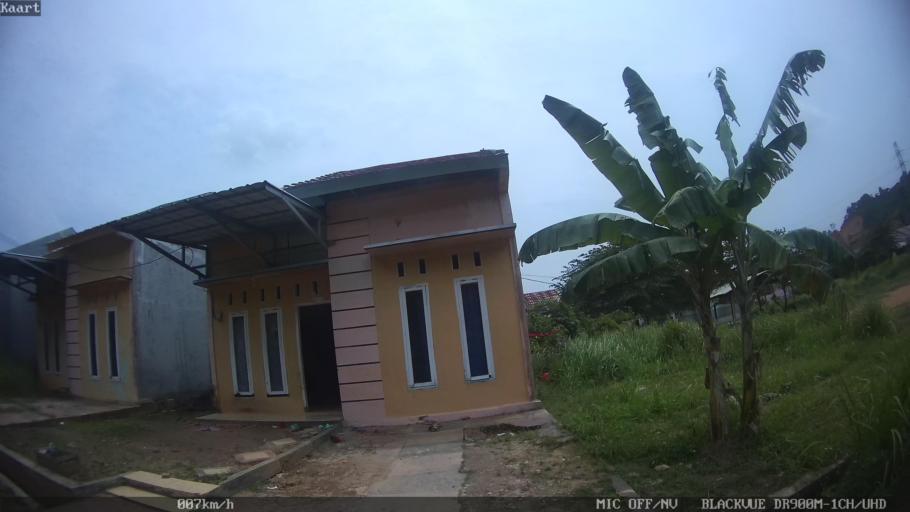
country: ID
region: Lampung
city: Kedaton
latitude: -5.4025
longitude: 105.3250
